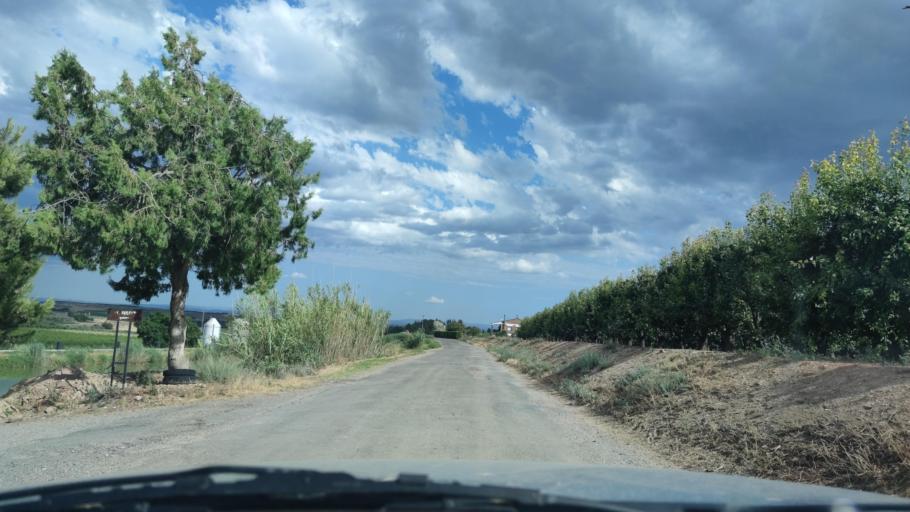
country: ES
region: Catalonia
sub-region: Provincia de Lleida
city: Alcarras
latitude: 41.6038
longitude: 0.5433
